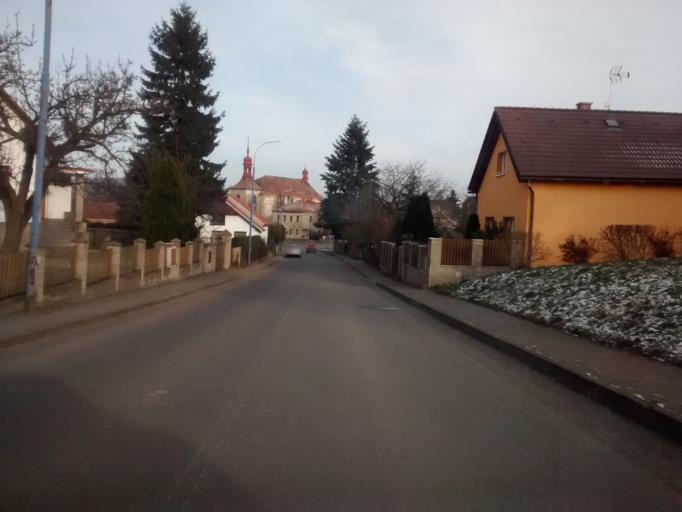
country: CZ
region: Ustecky
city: Velemin
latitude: 50.5362
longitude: 13.9764
